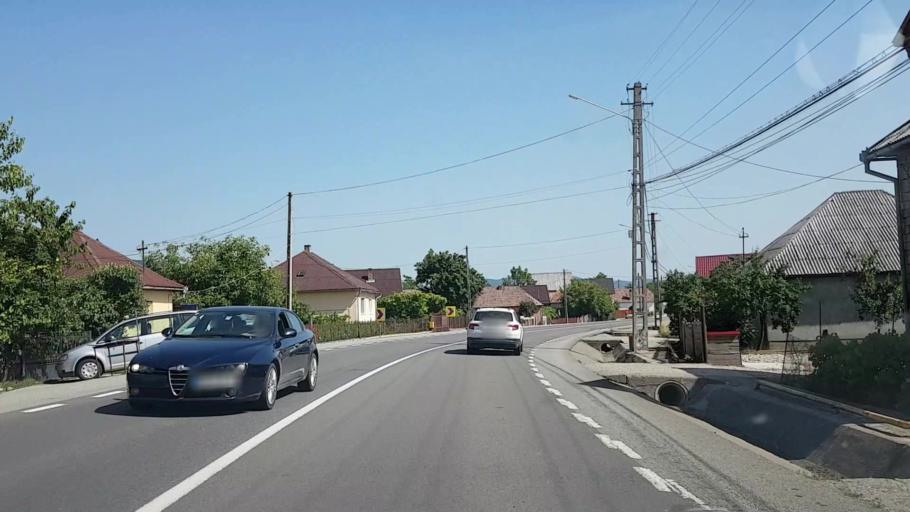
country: RO
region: Bistrita-Nasaud
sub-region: Comuna Sieu-Magherus
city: Sieu-Magherus
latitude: 47.0962
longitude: 24.3678
